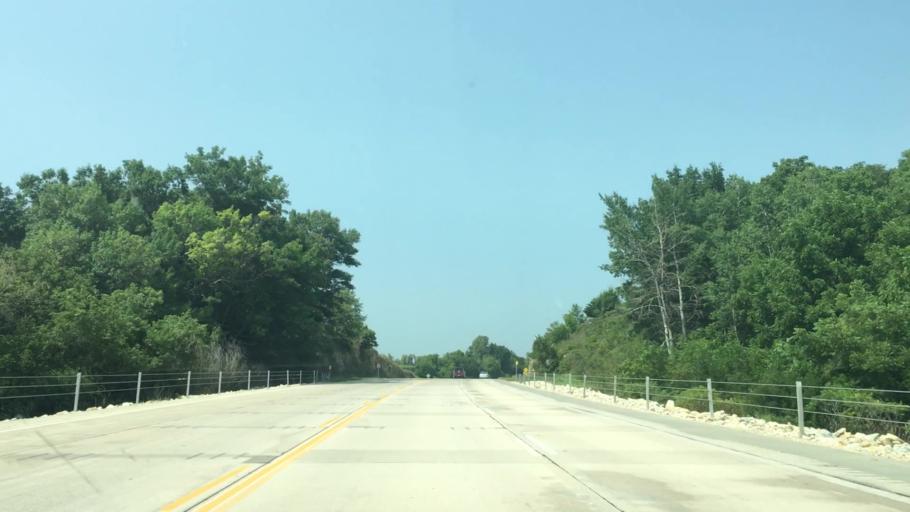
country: US
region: Iowa
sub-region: Winneshiek County
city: Decorah
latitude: 43.3037
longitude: -91.8147
